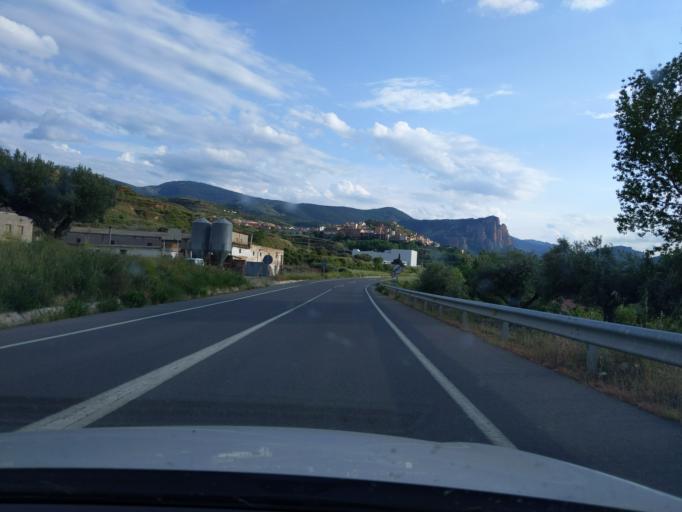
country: ES
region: La Rioja
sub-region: Provincia de La Rioja
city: Nalda
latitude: 42.3447
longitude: -2.4823
